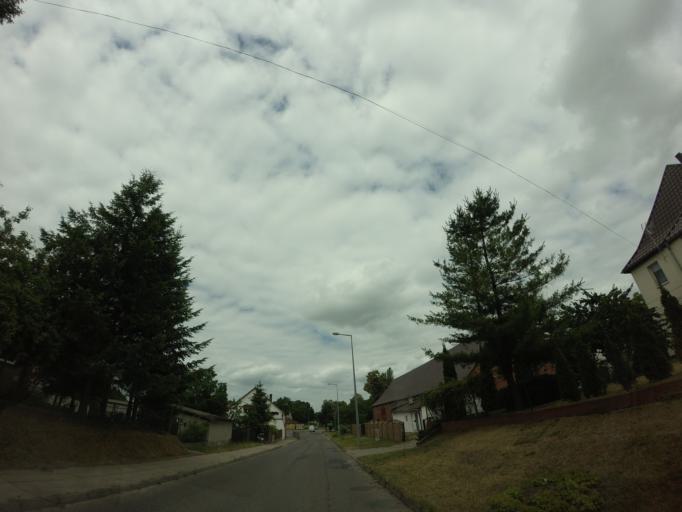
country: PL
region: Lubusz
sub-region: Powiat strzelecko-drezdenecki
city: Strzelce Krajenskie
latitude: 52.8802
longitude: 15.5429
